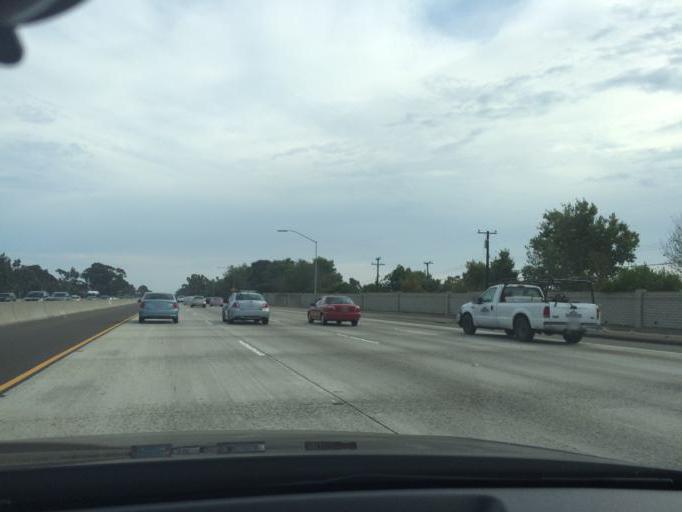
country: US
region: California
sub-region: San Diego County
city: San Diego
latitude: 32.7983
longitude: -117.1567
